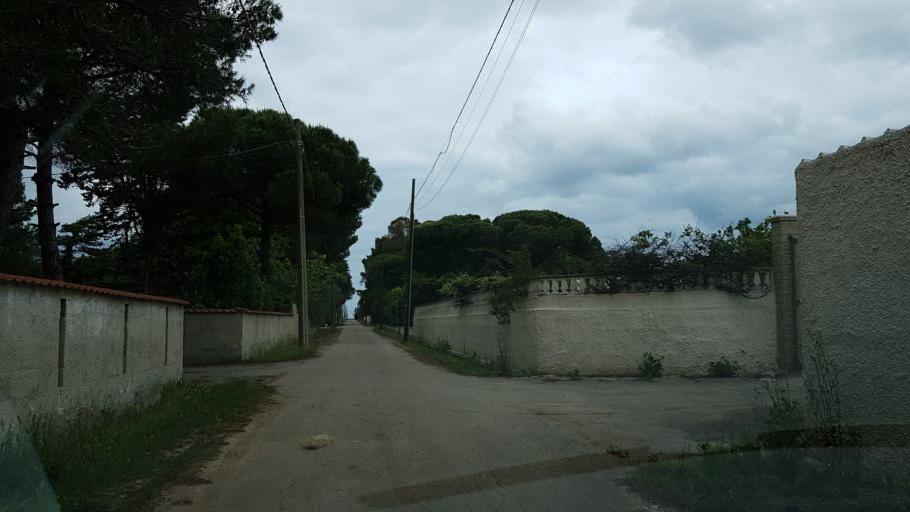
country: IT
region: Apulia
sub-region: Provincia di Brindisi
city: Brindisi
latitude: 40.6346
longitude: 17.8971
